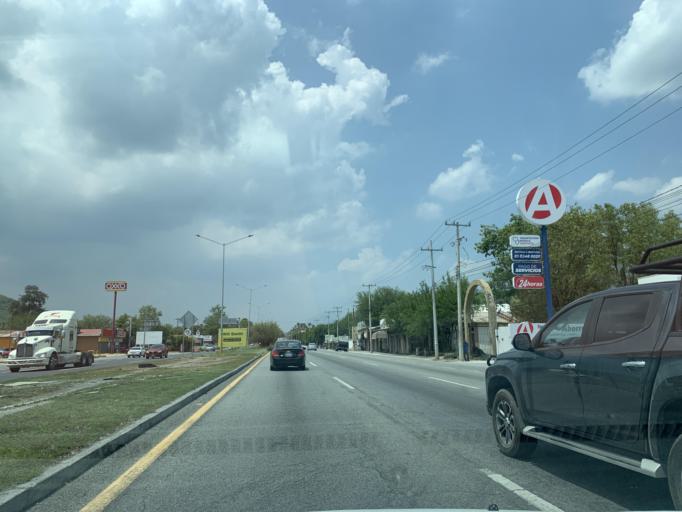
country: MX
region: Nuevo Leon
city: Santiago
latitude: 25.4609
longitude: -100.1700
